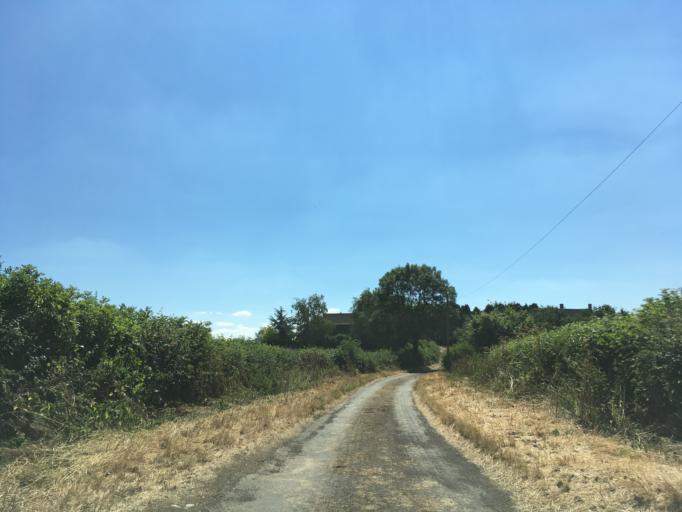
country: GB
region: England
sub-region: Wiltshire
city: Luckington
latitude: 51.5524
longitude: -2.2526
